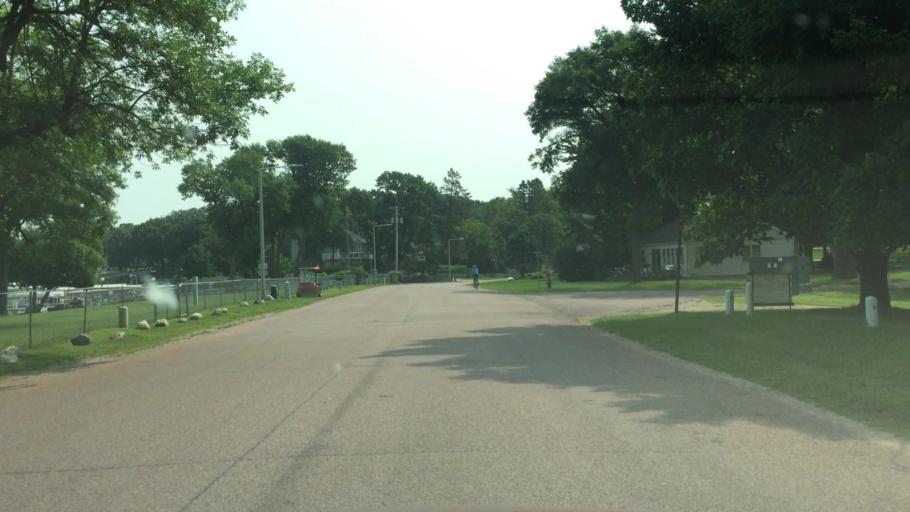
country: US
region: Iowa
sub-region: Dickinson County
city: Milford
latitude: 43.3492
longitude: -95.1541
